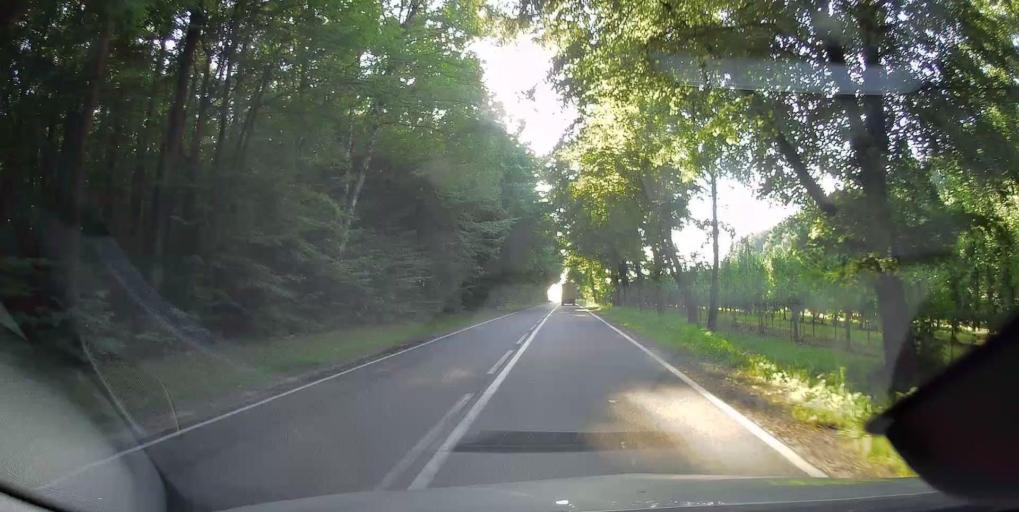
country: PL
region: Lodz Voivodeship
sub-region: Powiat rawski
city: Sadkowice
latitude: 51.8047
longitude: 20.5874
